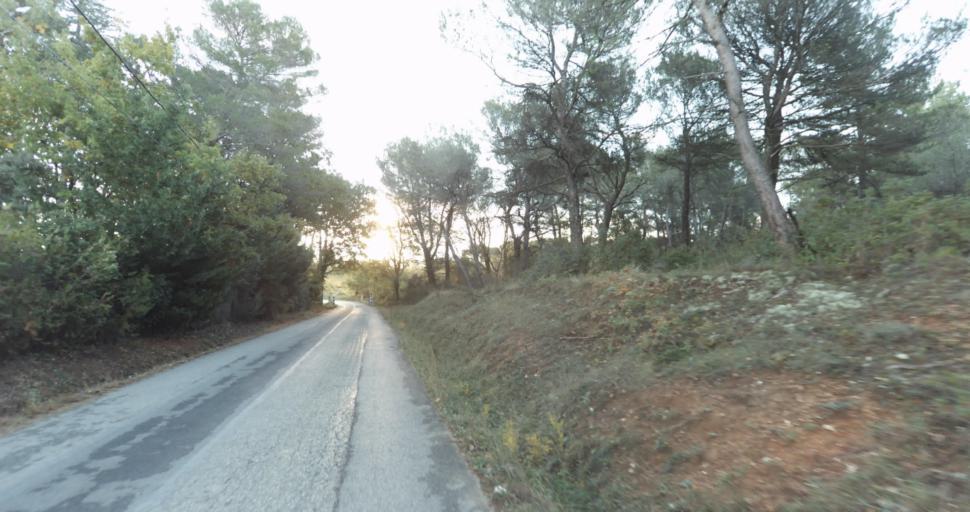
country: FR
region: Provence-Alpes-Cote d'Azur
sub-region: Departement des Bouches-du-Rhone
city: Venelles
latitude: 43.5762
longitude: 5.4888
